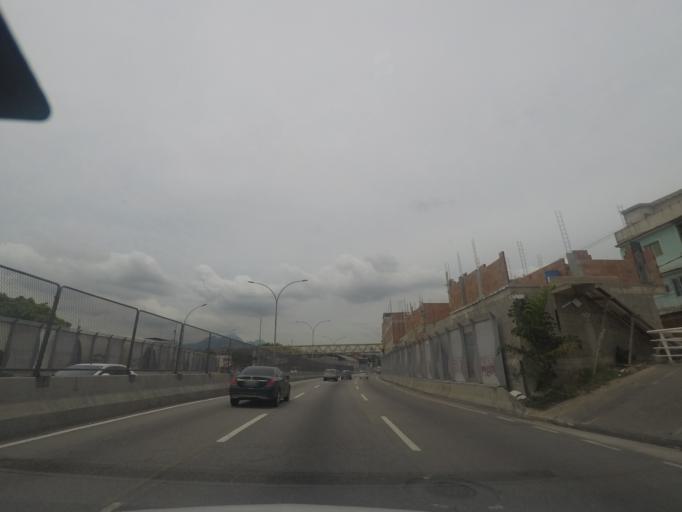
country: BR
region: Rio de Janeiro
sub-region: Rio De Janeiro
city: Rio de Janeiro
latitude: -22.8680
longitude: -43.2413
